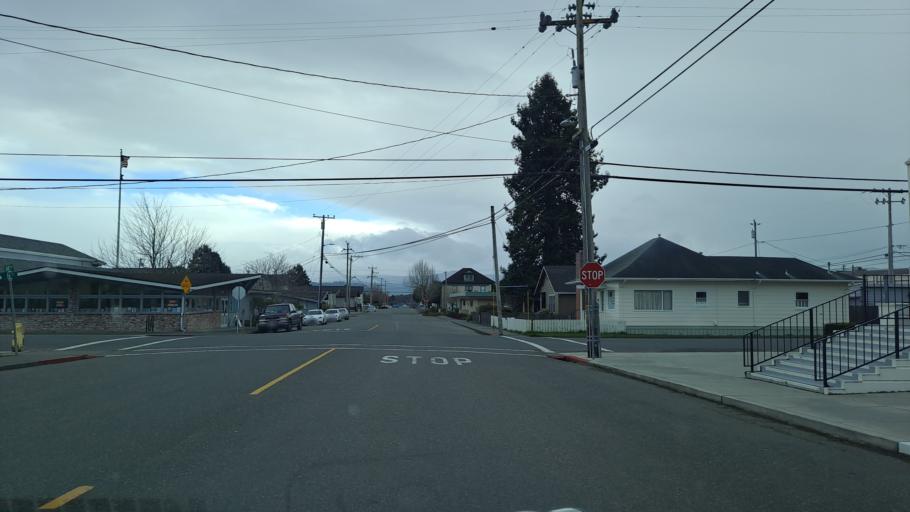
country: US
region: California
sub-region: Humboldt County
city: Fortuna
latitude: 40.5991
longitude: -124.1523
